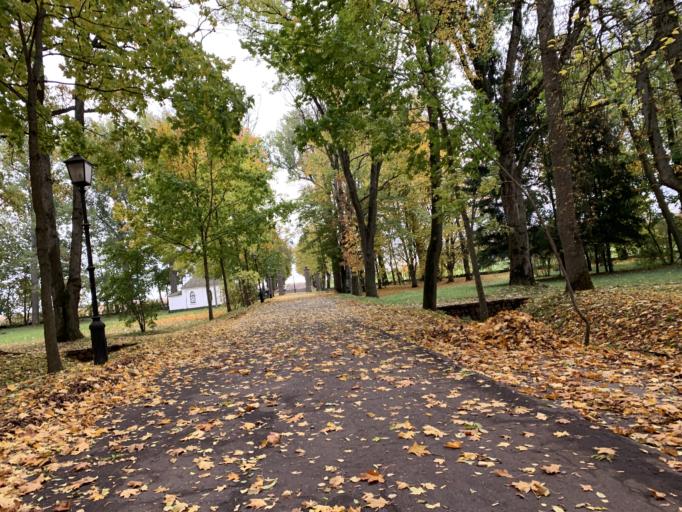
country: BY
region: Minsk
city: Nyasvizh
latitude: 53.2217
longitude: 26.7007
